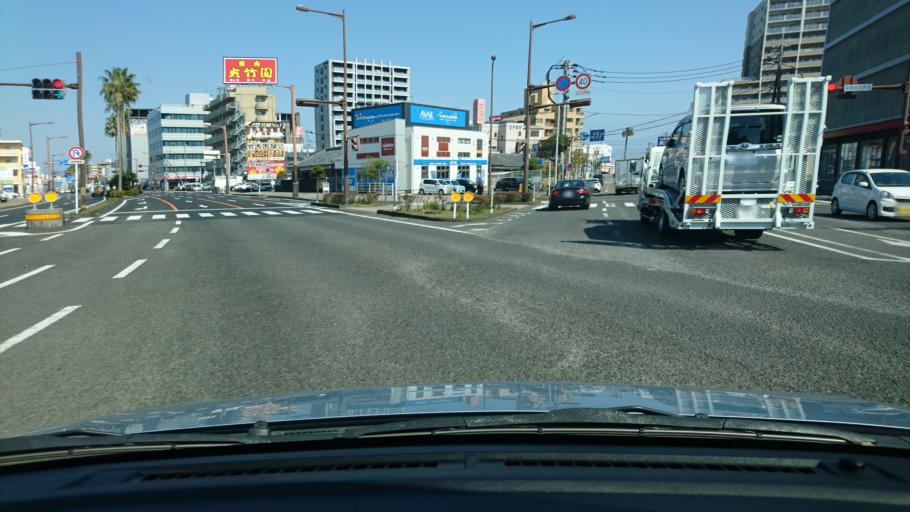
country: JP
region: Miyazaki
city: Miyazaki-shi
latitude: 31.8930
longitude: 131.4161
